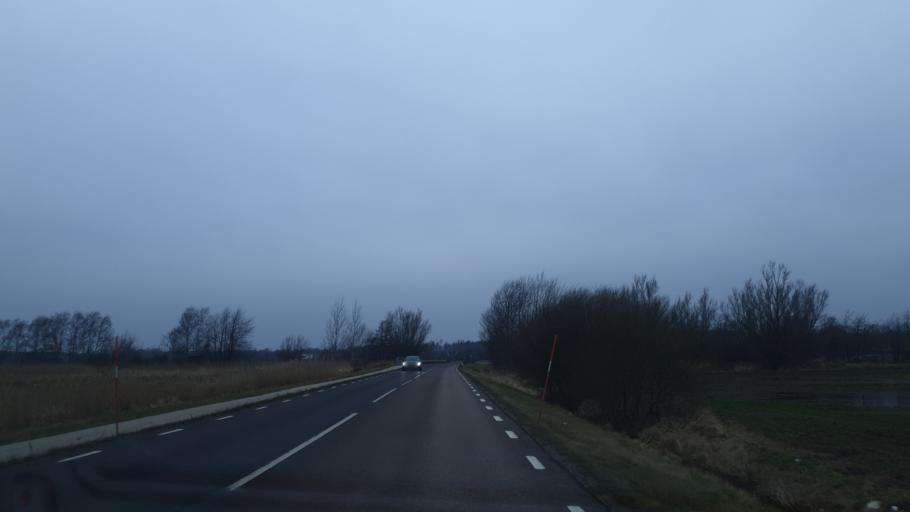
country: SE
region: Blekinge
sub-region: Karlskrona Kommun
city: Jaemjoe
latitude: 56.1728
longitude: 15.7282
